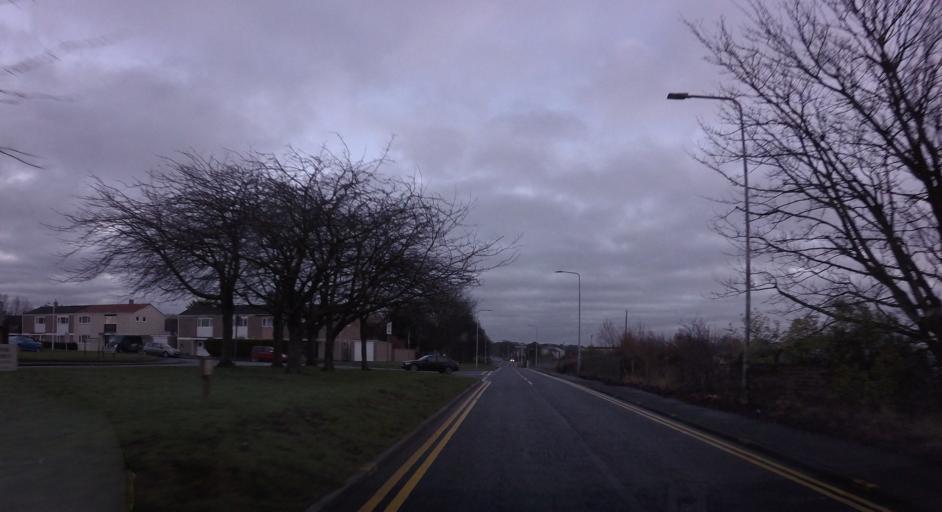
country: GB
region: Scotland
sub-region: Fife
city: Rosyth
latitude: 56.0304
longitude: -3.4415
